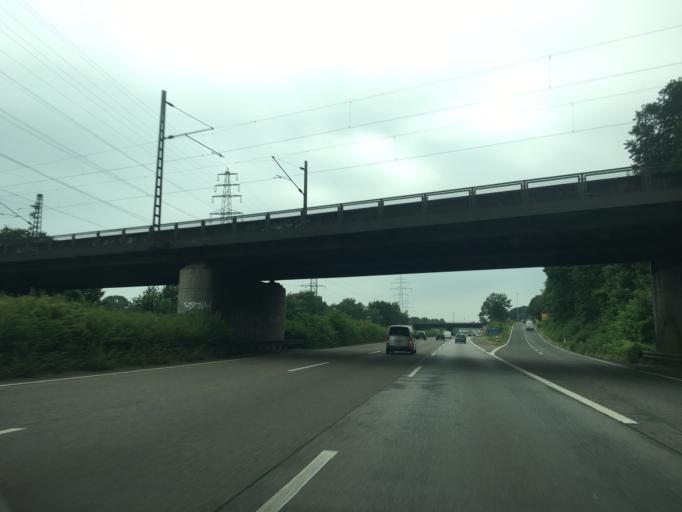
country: DE
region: North Rhine-Westphalia
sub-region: Regierungsbezirk Dusseldorf
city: Oberhausen
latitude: 51.4963
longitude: 6.8696
